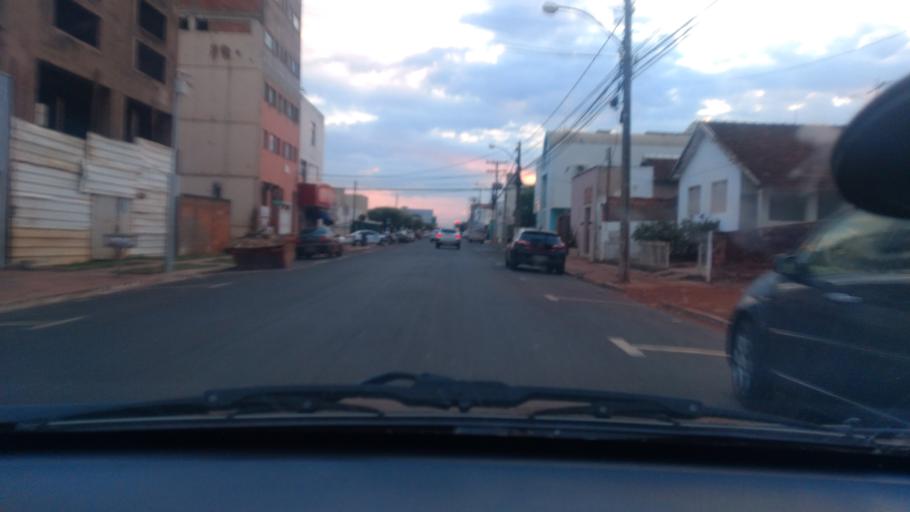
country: BR
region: Goias
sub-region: Santa Helena De Goias
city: Santa Helena de Goias
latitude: -17.7952
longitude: -50.9275
